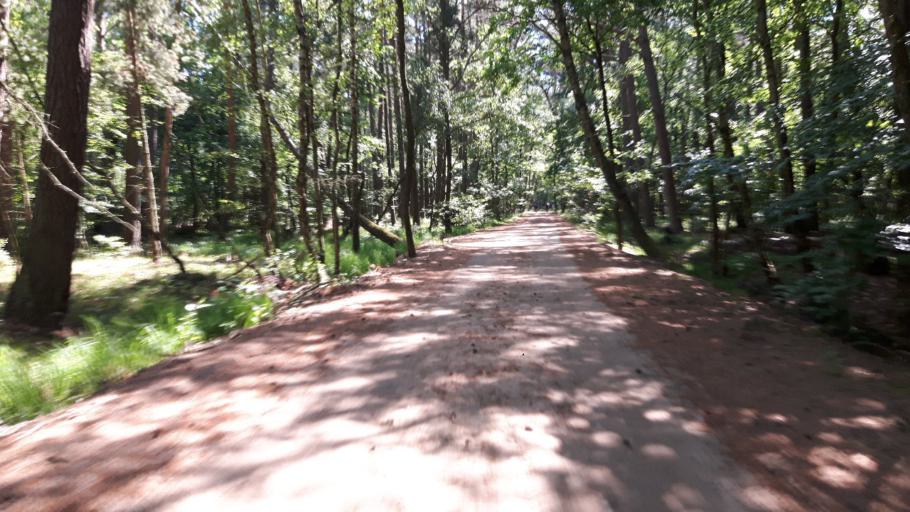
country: PL
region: Pomeranian Voivodeship
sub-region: Powiat slupski
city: Smoldzino
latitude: 54.6780
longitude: 17.1503
